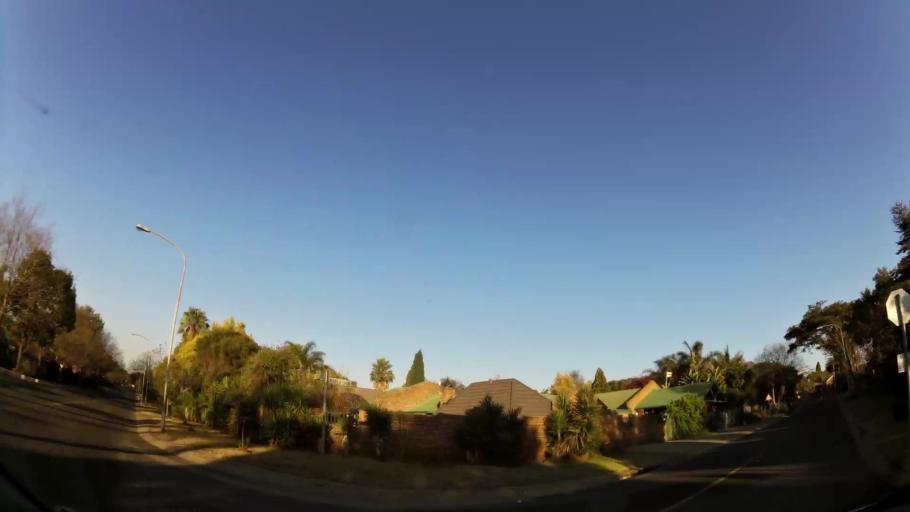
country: ZA
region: Gauteng
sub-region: City of Tshwane Metropolitan Municipality
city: Centurion
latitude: -25.8719
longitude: 28.1459
